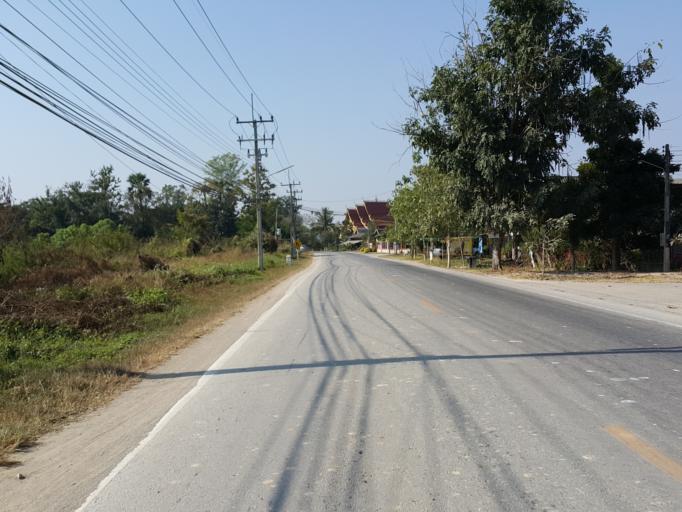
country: TH
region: Lamphun
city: Ban Thi
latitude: 18.6699
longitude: 99.1380
